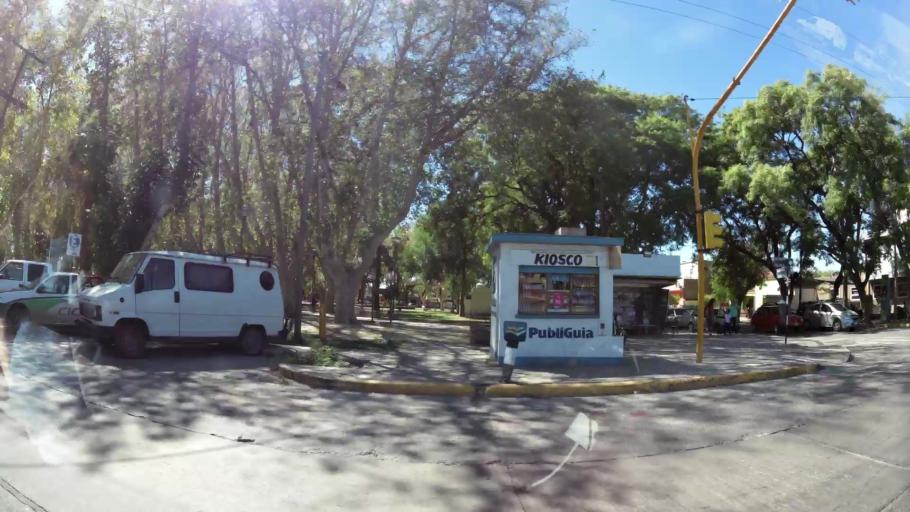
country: AR
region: San Juan
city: Villa Krause
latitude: -31.5522
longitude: -68.5228
